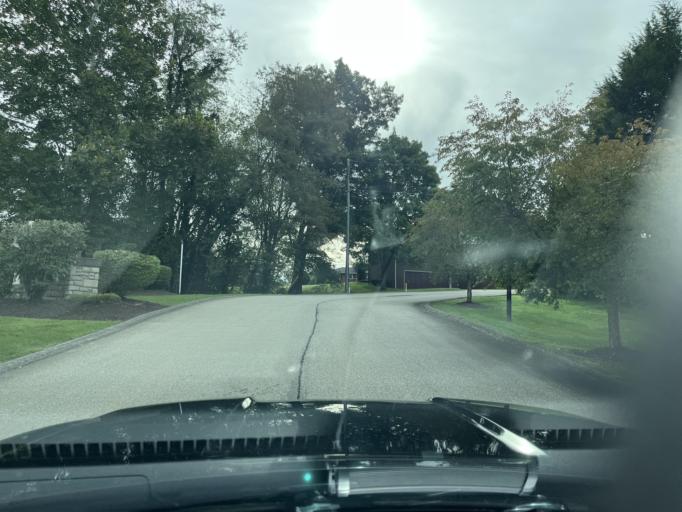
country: US
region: Pennsylvania
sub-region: Fayette County
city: South Uniontown
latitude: 39.8857
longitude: -79.7415
